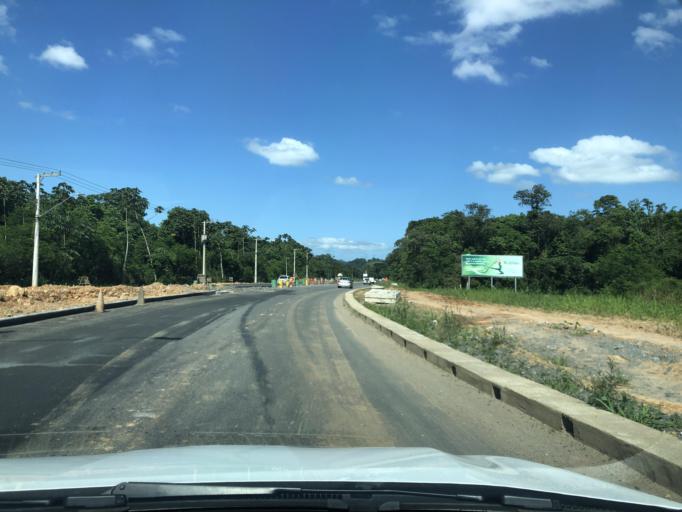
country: BR
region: Santa Catarina
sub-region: Joinville
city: Joinville
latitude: -26.2505
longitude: -48.8632
